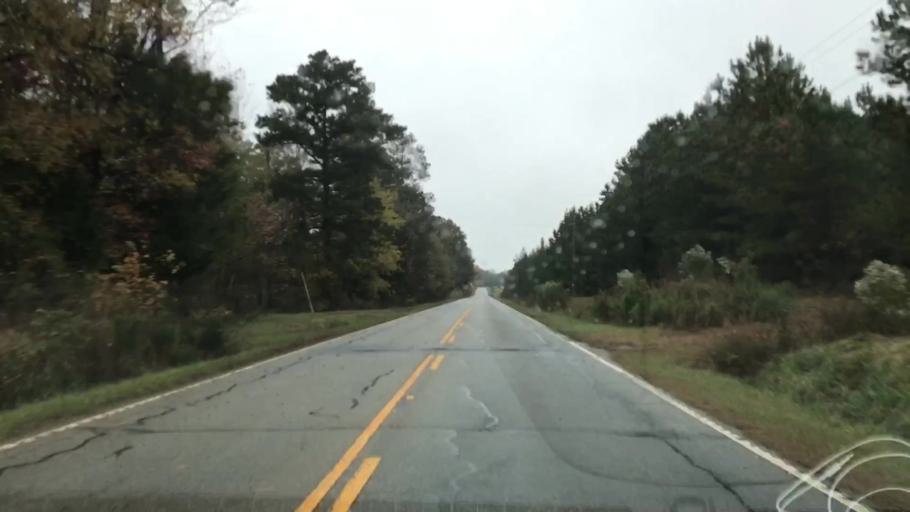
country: US
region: South Carolina
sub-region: Laurens County
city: Joanna
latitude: 34.3618
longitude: -81.7422
